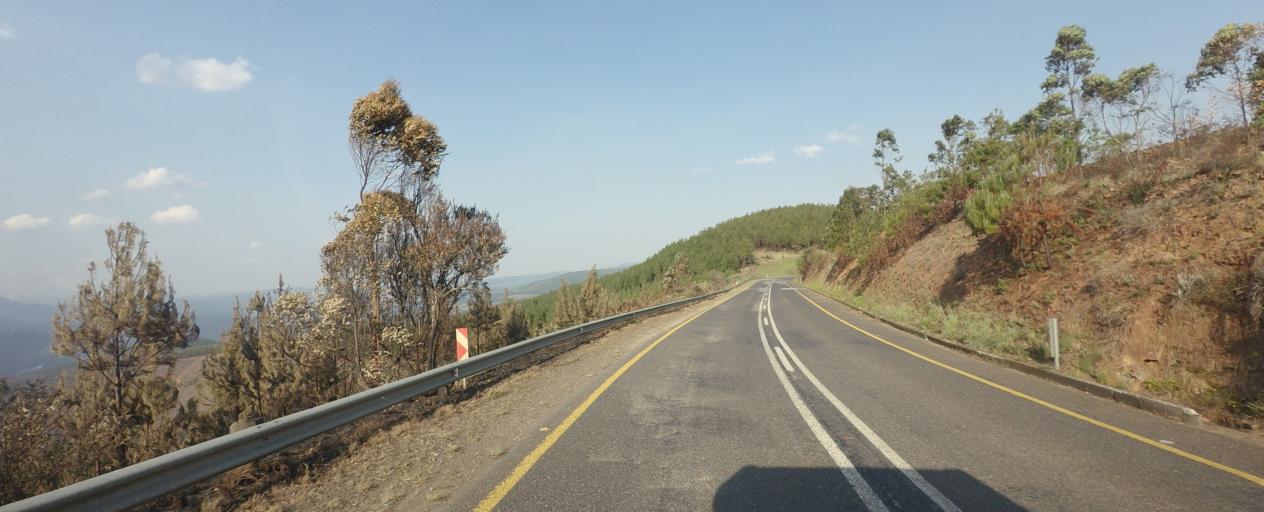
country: ZA
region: Mpumalanga
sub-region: Ehlanzeni District
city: Lydenburg
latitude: -25.1646
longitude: 30.6871
